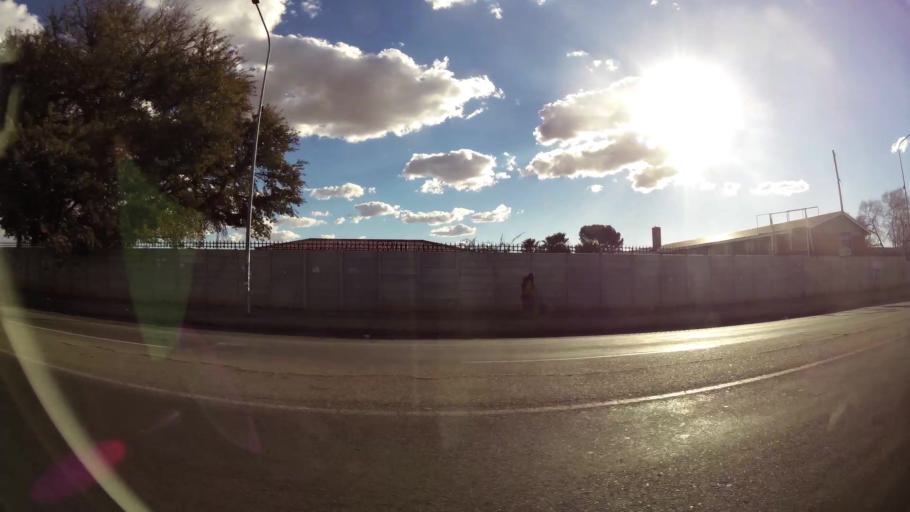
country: ZA
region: North-West
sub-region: Dr Kenneth Kaunda District Municipality
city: Klerksdorp
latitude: -26.8744
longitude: 26.6647
